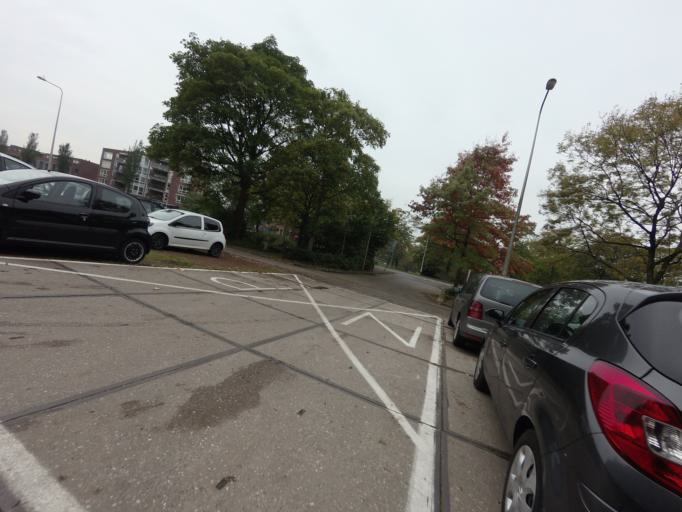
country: NL
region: Utrecht
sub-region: Gemeente Vianen
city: Vianen
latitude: 51.9922
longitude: 5.0968
